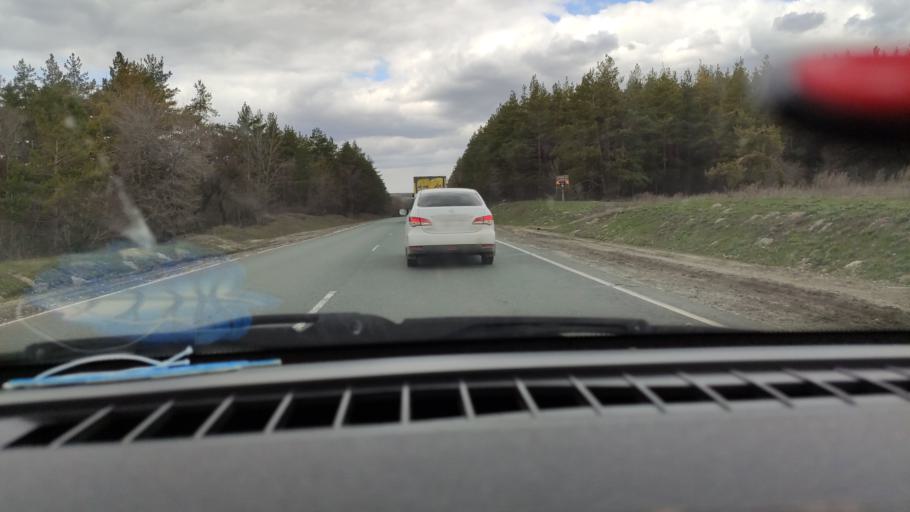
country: RU
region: Saratov
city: Vol'sk
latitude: 52.1052
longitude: 47.4372
